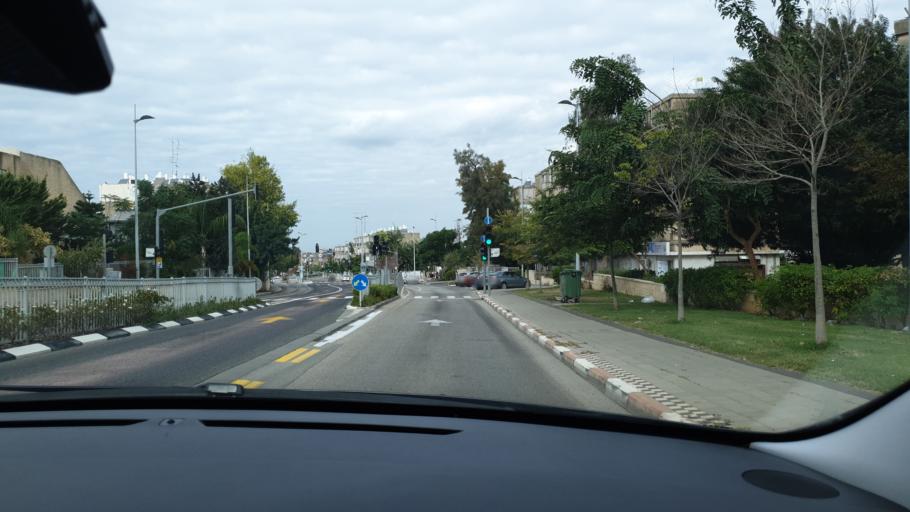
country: IL
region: Haifa
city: Qiryat Ata
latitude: 32.8121
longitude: 35.1146
